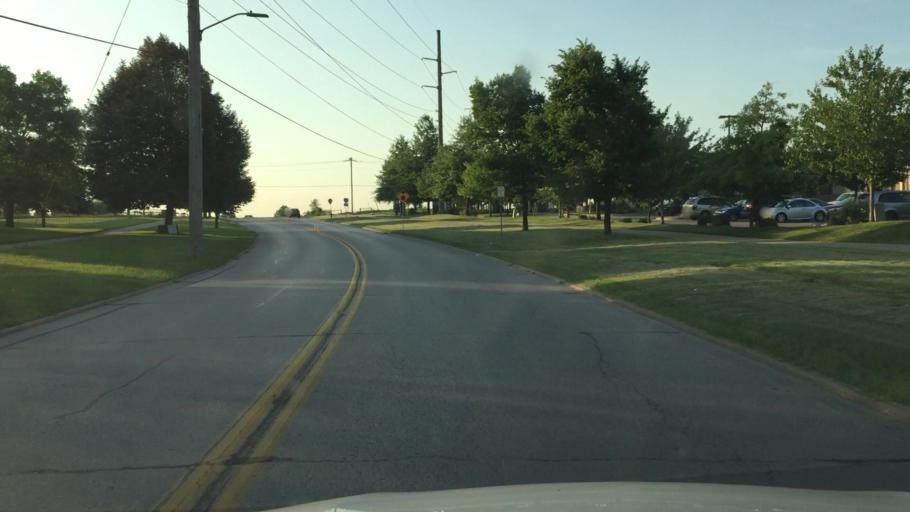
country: US
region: Iowa
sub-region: Johnson County
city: Iowa City
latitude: 41.6673
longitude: -91.4830
